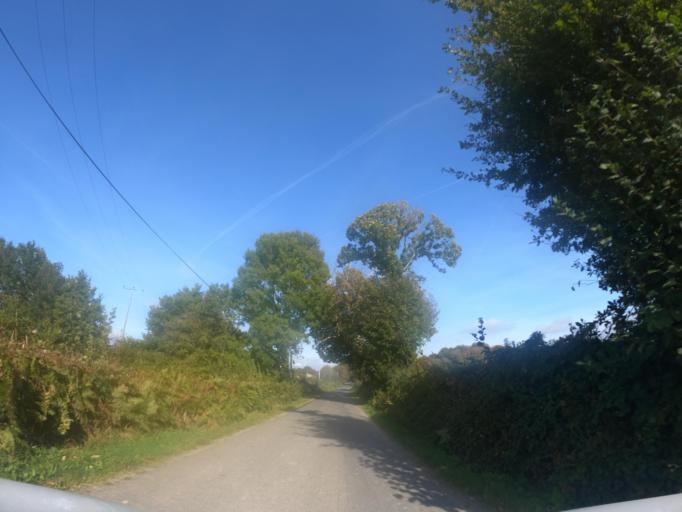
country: FR
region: Poitou-Charentes
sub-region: Departement des Deux-Sevres
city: Courlay
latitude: 46.7906
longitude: -0.5631
